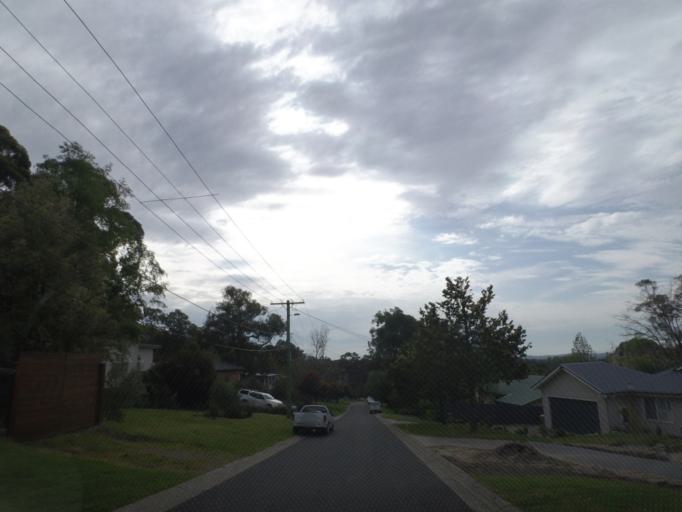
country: AU
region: Victoria
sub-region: Knox
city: The Basin
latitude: -37.8600
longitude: 145.3213
